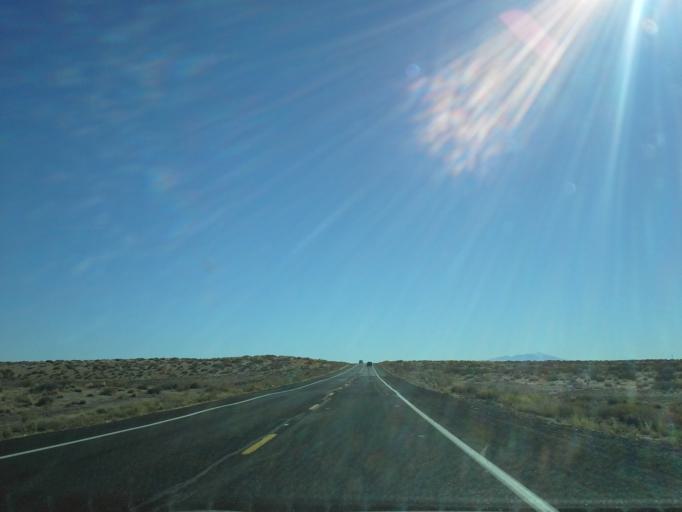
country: US
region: Arizona
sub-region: Coconino County
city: Tuba City
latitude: 35.9720
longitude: -111.3959
